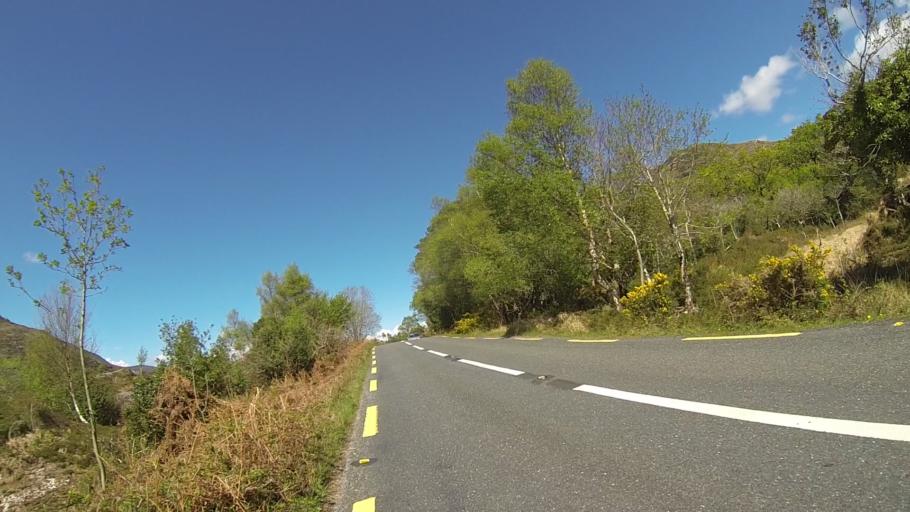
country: IE
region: Munster
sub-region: Ciarrai
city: Cill Airne
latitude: 51.9916
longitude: -9.5533
